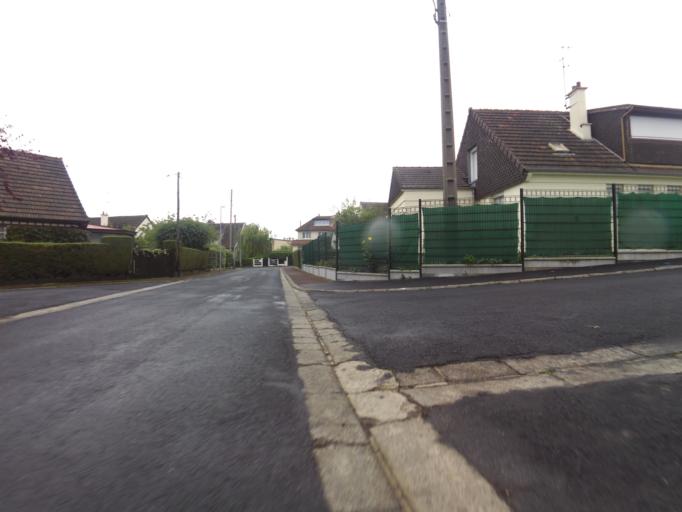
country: FR
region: Lower Normandy
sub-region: Departement du Calvados
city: Caen
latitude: 49.1942
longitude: -0.3524
